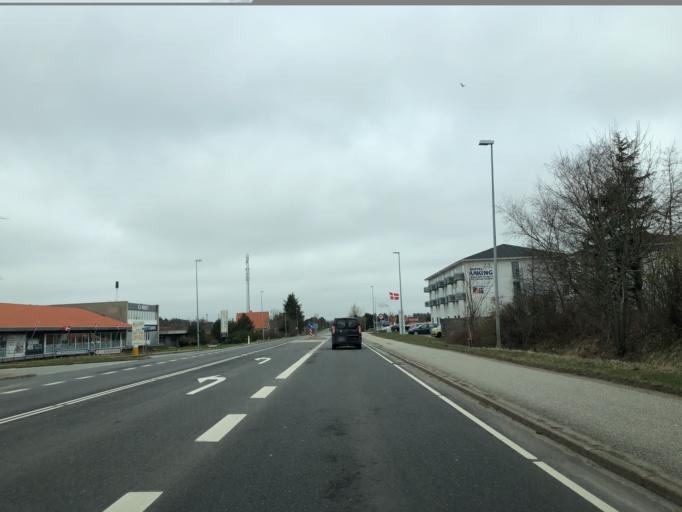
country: DK
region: North Denmark
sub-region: Frederikshavn Kommune
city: Saeby
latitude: 57.3448
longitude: 10.5144
